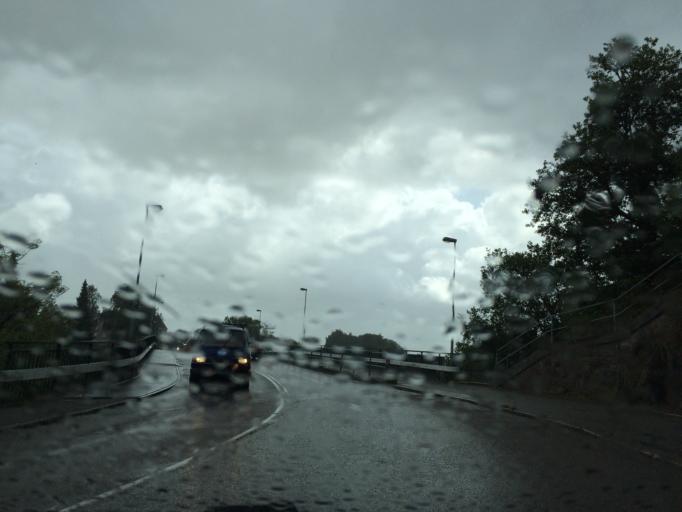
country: SE
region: Vaestra Goetaland
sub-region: Trollhattan
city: Trollhattan
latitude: 58.2867
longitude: 12.2815
